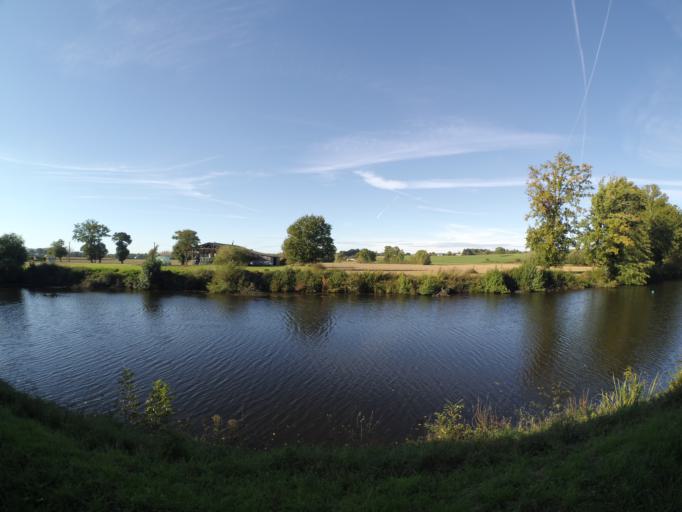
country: FR
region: Brittany
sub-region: Departement du Morbihan
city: Saint-Martin-sur-Oust
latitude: 47.7386
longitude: -2.2433
